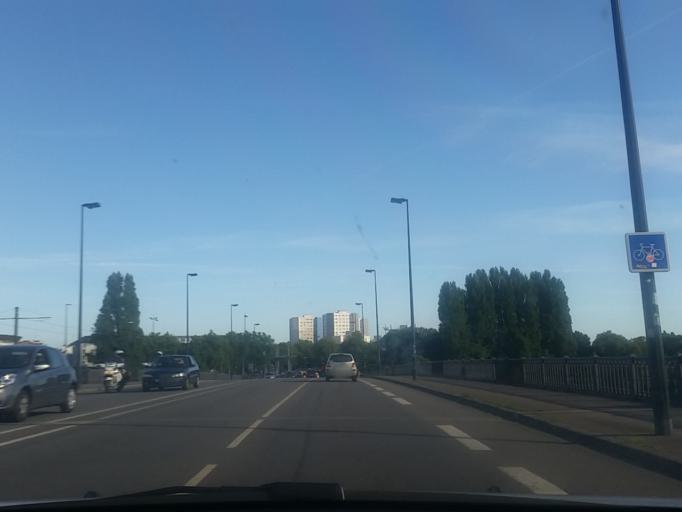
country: FR
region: Pays de la Loire
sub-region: Departement de la Loire-Atlantique
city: Reze
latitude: 47.1994
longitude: -1.5436
